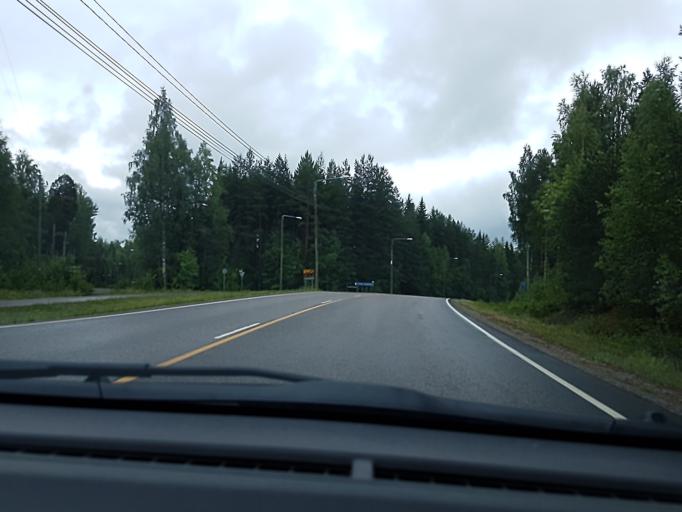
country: FI
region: Uusimaa
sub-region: Helsinki
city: Pornainen
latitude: 60.4650
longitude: 25.3900
